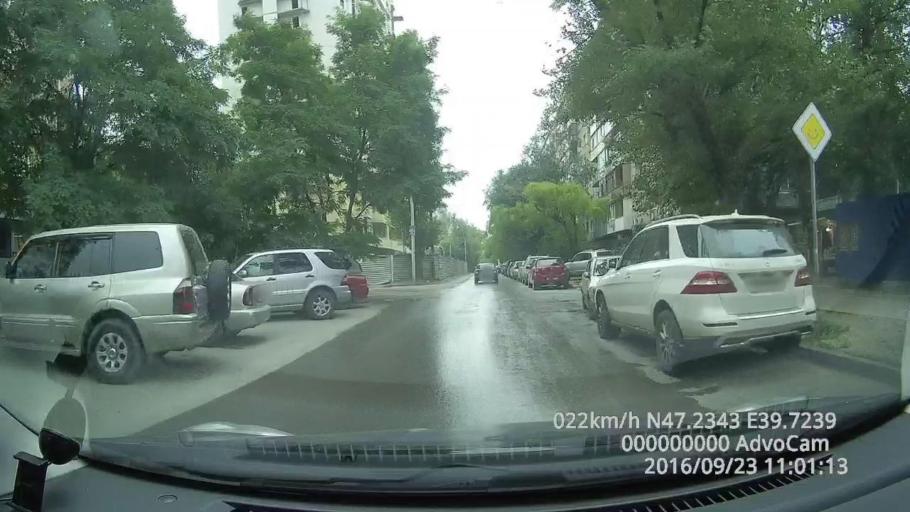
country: RU
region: Rostov
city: Rostov-na-Donu
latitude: 47.2344
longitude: 39.7239
